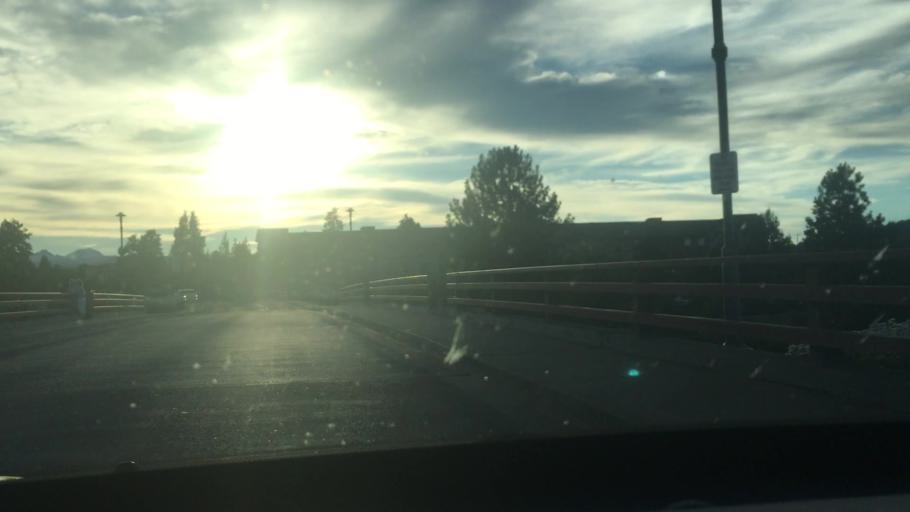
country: US
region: Oregon
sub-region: Deschutes County
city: Bend
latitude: 44.0432
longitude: -121.3161
